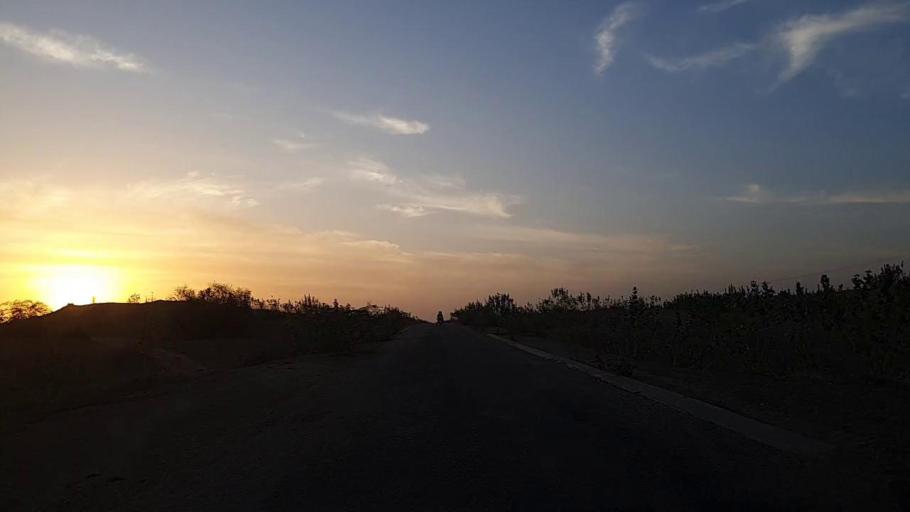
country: PK
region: Sindh
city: Nabisar
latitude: 24.9852
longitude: 69.8975
